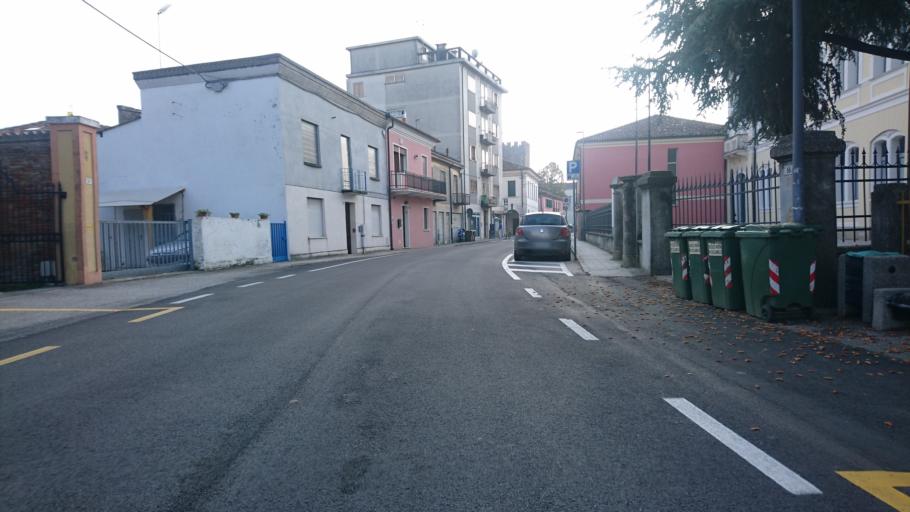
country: IT
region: Veneto
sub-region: Provincia di Rovigo
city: Arqua Polesine
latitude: 45.0110
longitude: 11.7414
